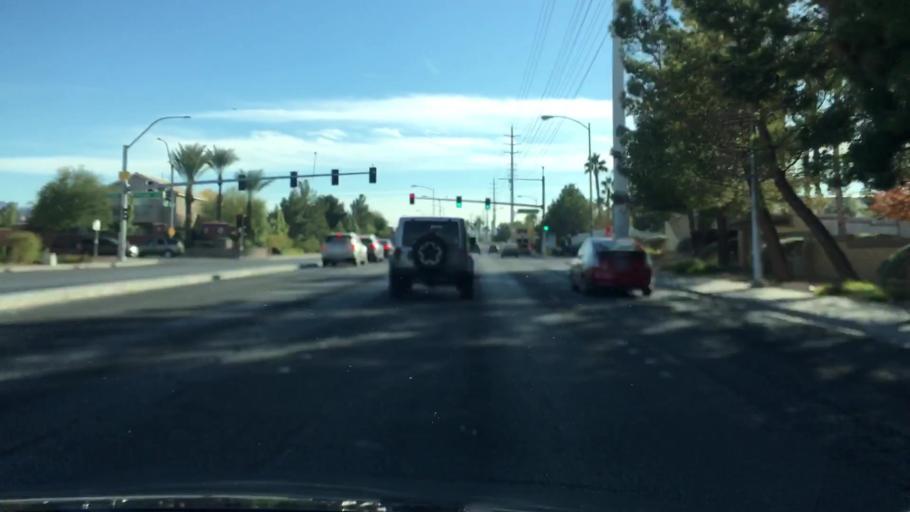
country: US
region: Nevada
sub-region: Clark County
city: Whitney
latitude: 36.0140
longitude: -115.1189
